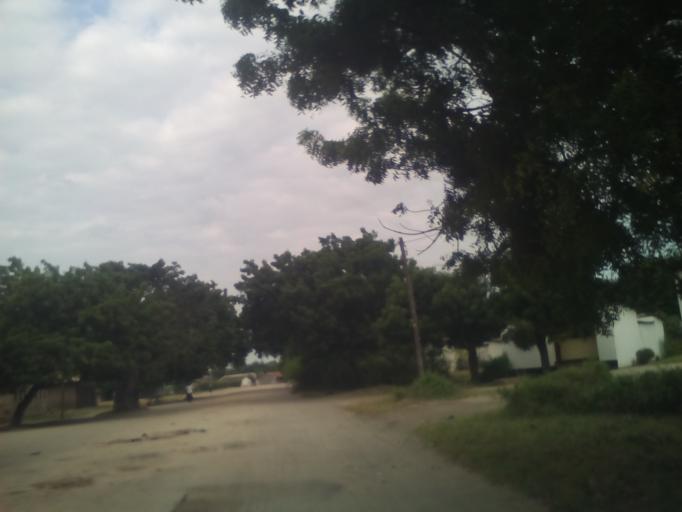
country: TZ
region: Dar es Salaam
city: Dar es Salaam
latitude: -6.8479
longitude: 39.2768
